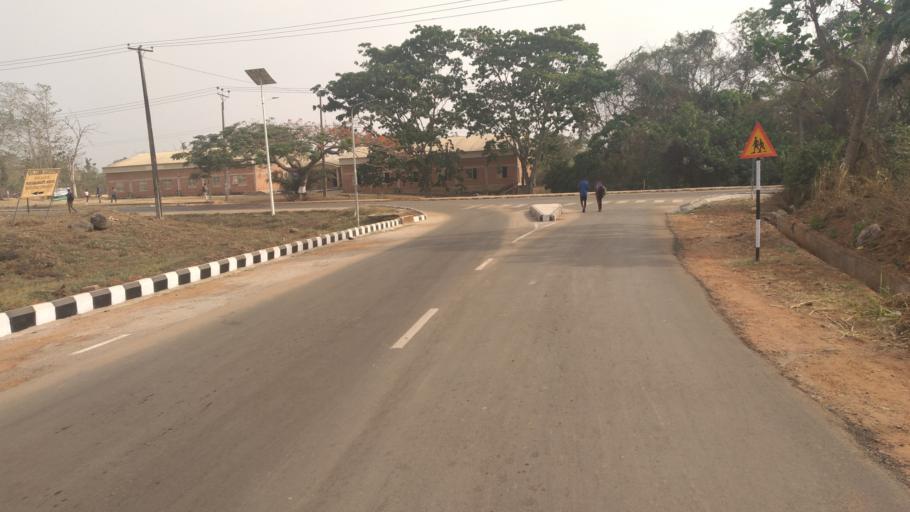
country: NG
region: Ondo
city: Ilare
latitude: 7.2968
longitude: 5.1457
